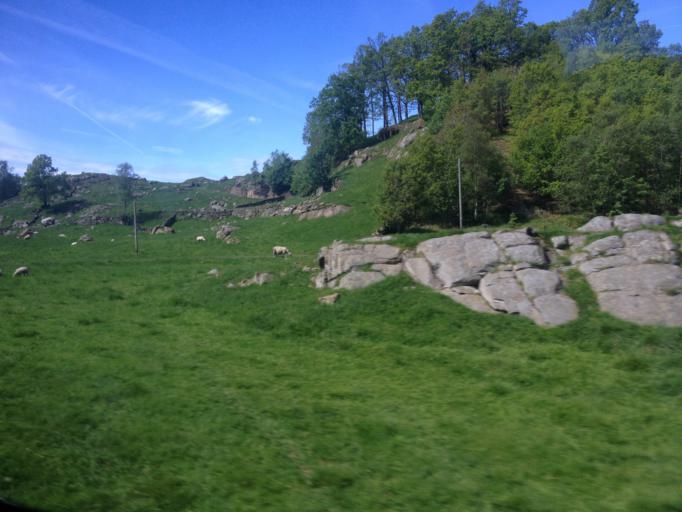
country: NO
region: Rogaland
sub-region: Bjerkreim
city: Vikesa
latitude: 58.5401
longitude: 6.2079
